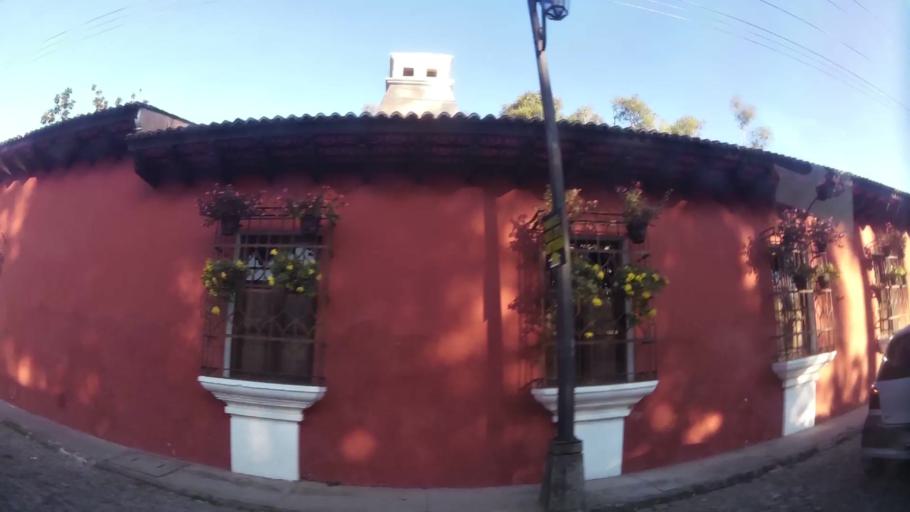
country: GT
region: Sacatepequez
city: Antigua Guatemala
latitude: 14.5530
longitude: -90.7332
